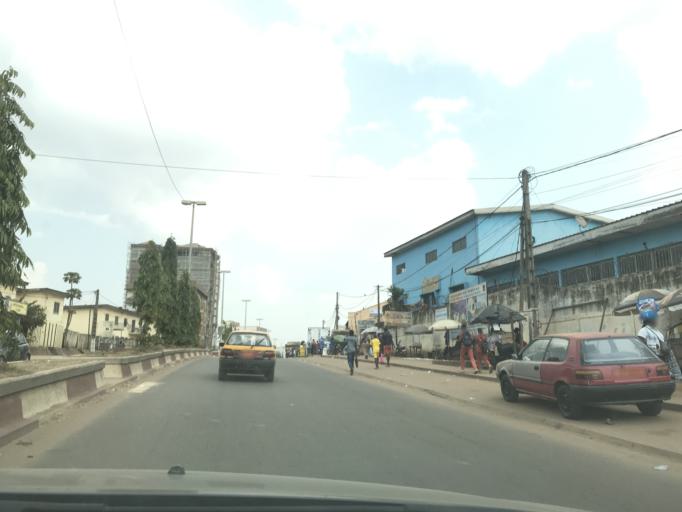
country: CM
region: Centre
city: Yaounde
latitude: 3.8889
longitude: 11.5233
